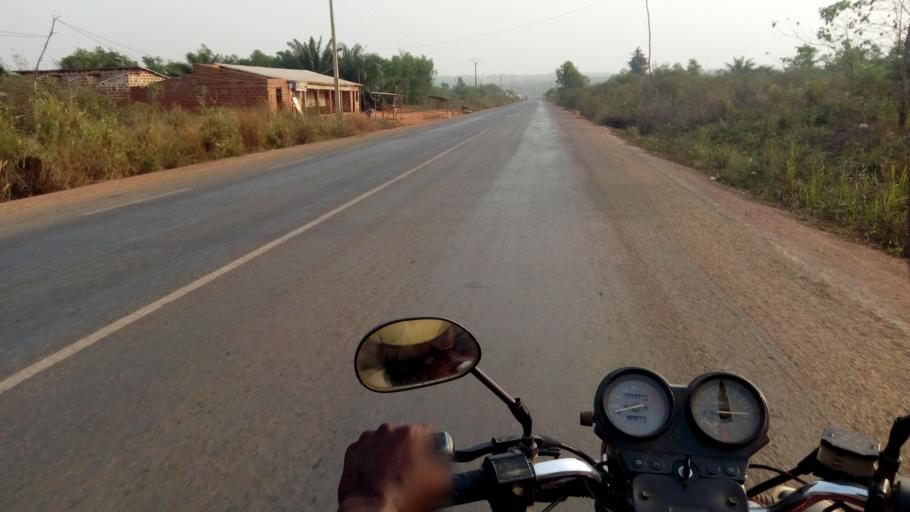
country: BJ
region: Atlantique
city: Hinvi
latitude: 6.7022
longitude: 2.2899
